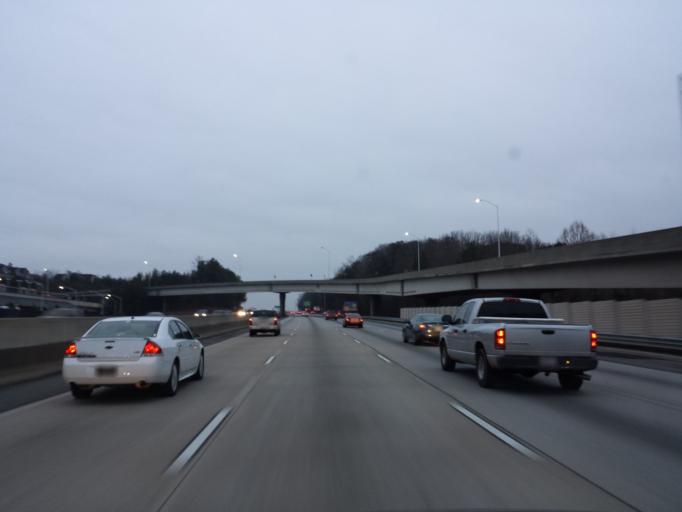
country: US
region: Georgia
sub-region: DeKalb County
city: Dunwoody
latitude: 33.9462
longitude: -84.3581
